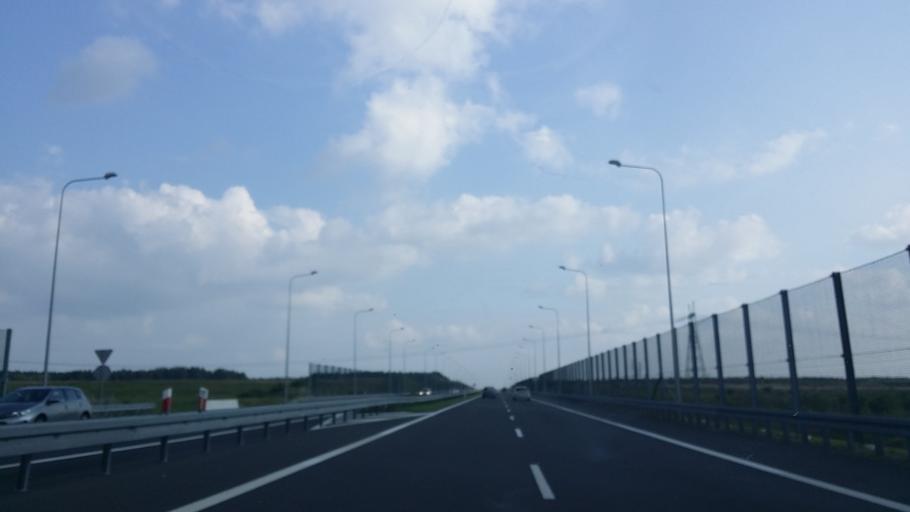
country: PL
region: Lubusz
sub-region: Powiat miedzyrzecki
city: Skwierzyna
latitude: 52.5446
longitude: 15.5407
